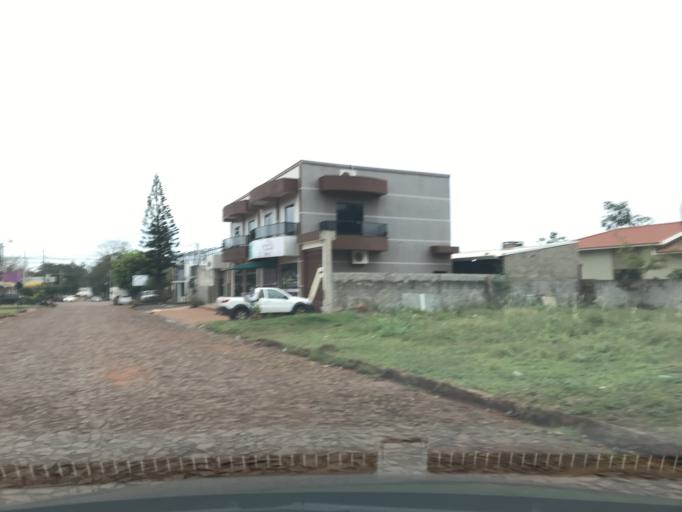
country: PY
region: Canindeyu
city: Colonia Catuete
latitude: -24.2479
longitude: -54.7595
